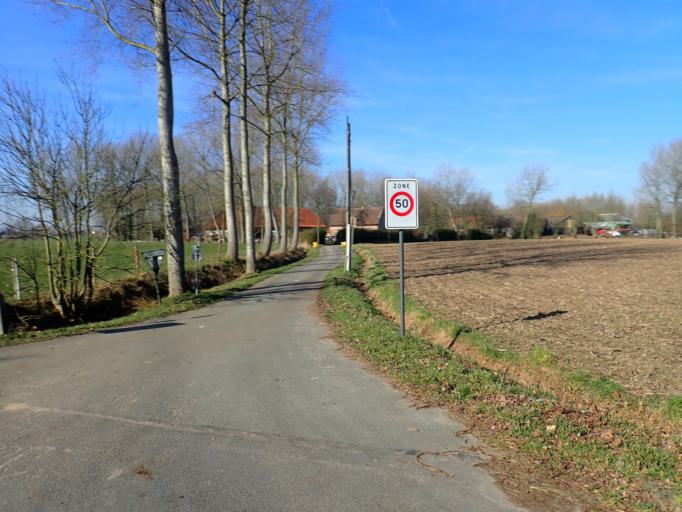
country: BE
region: Flanders
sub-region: Provincie Oost-Vlaanderen
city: Kruibeke
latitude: 51.1379
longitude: 4.2858
